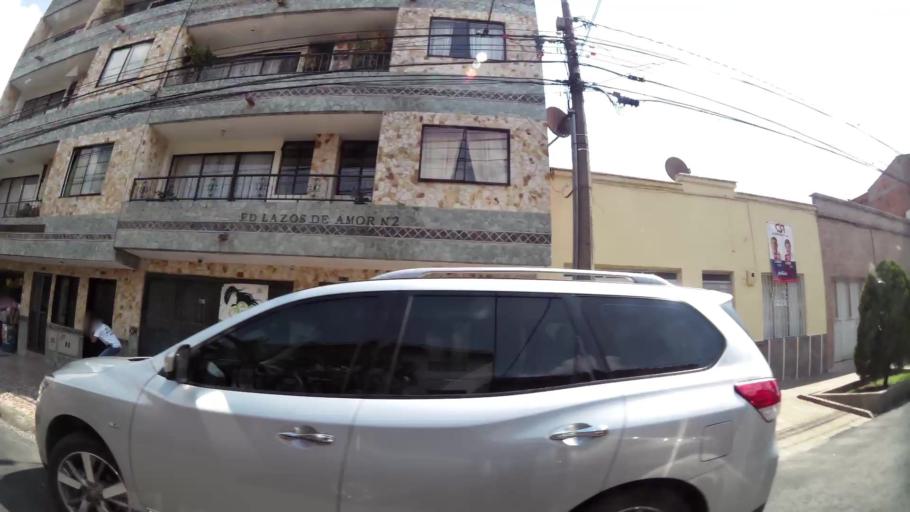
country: CO
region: Antioquia
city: Medellin
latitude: 6.2297
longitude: -75.5931
